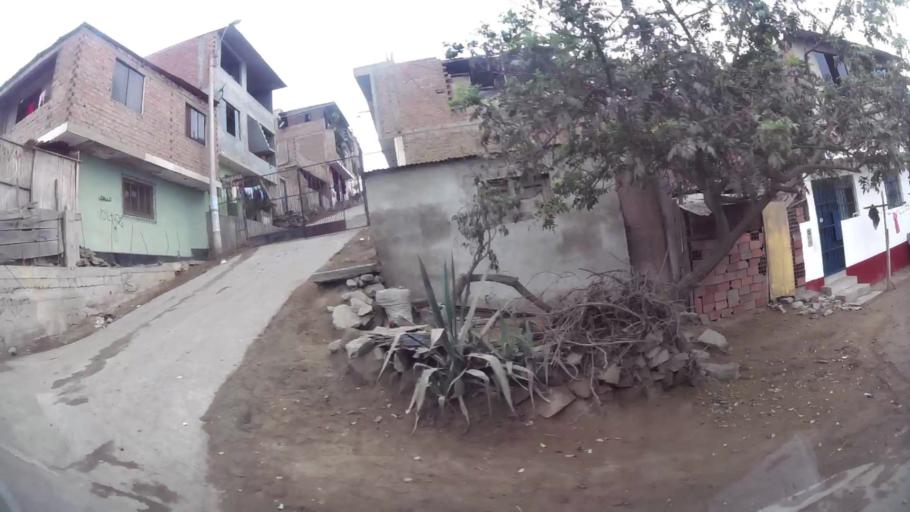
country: PE
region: Lima
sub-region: Lima
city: Surco
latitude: -12.1707
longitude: -76.9580
